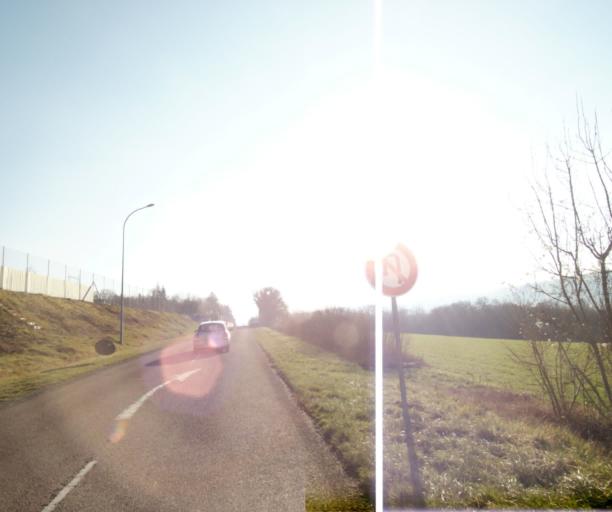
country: FR
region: Champagne-Ardenne
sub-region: Departement de la Haute-Marne
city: Chevillon
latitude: 48.5180
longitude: 5.1184
